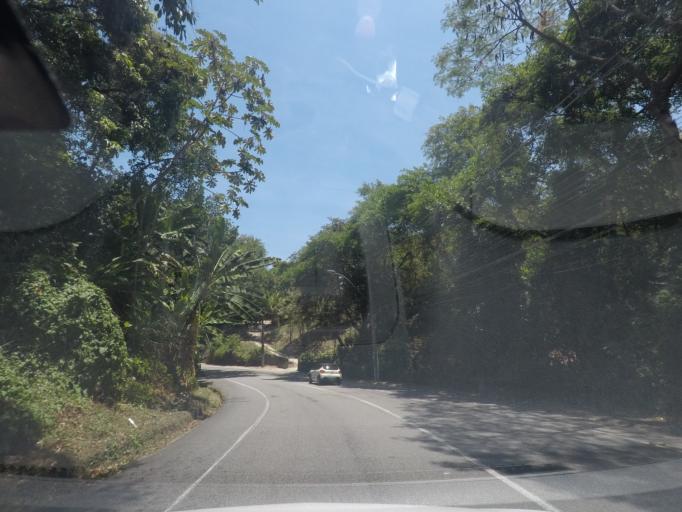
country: BR
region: Rio de Janeiro
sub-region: Niteroi
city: Niteroi
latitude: -22.9229
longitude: -43.0667
